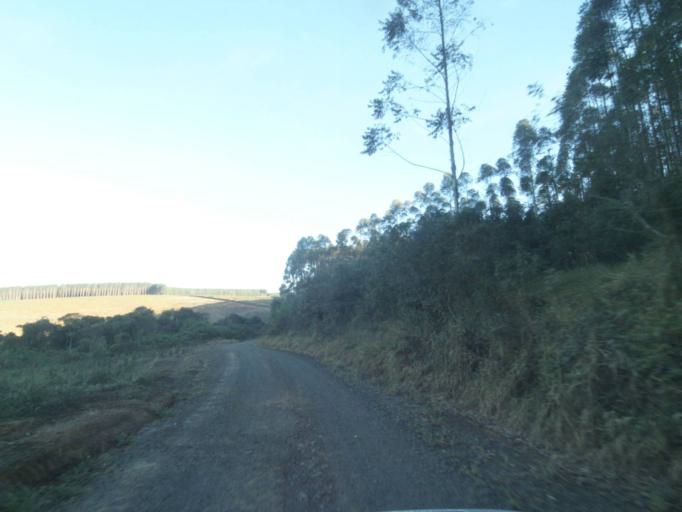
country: BR
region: Parana
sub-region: Telemaco Borba
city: Telemaco Borba
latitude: -24.4415
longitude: -50.6000
